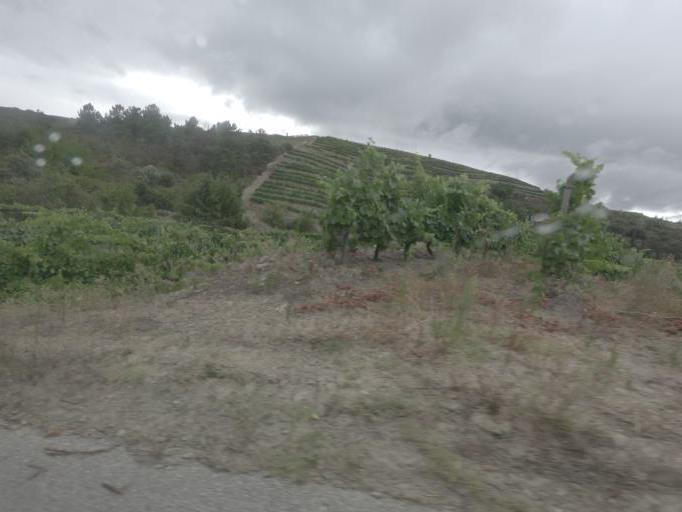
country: PT
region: Vila Real
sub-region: Sabrosa
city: Sabrosa
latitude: 41.2363
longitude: -7.4948
